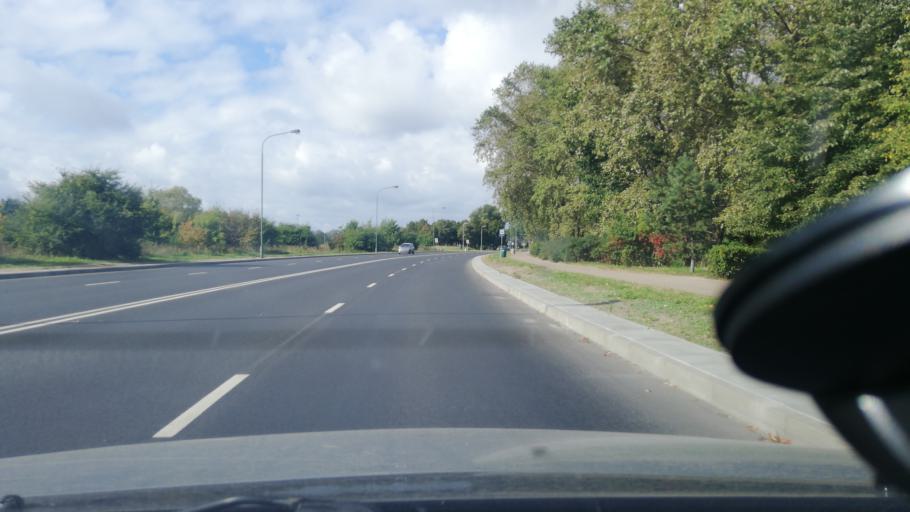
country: LT
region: Klaipedos apskritis
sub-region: Klaipeda
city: Klaipeda
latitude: 55.6654
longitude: 21.1666
